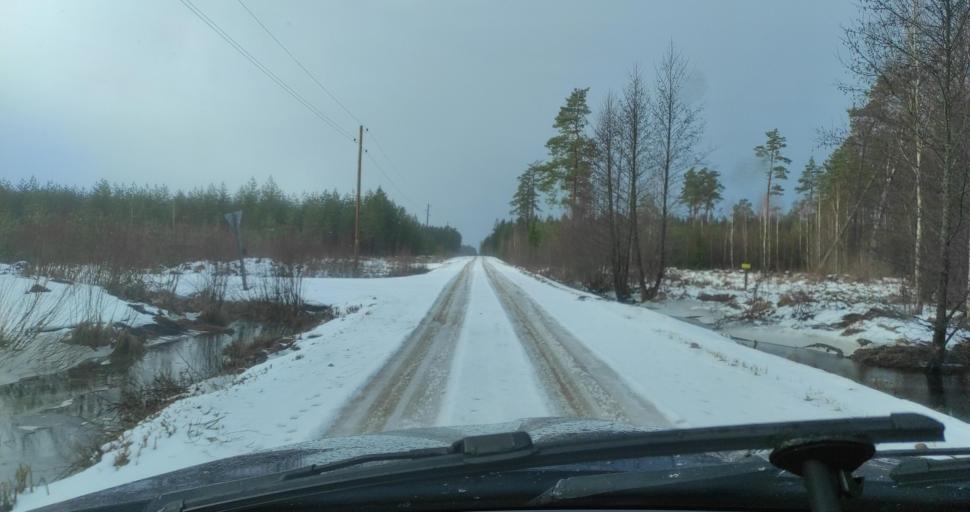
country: LV
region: Dundaga
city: Dundaga
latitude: 57.3820
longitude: 22.1533
